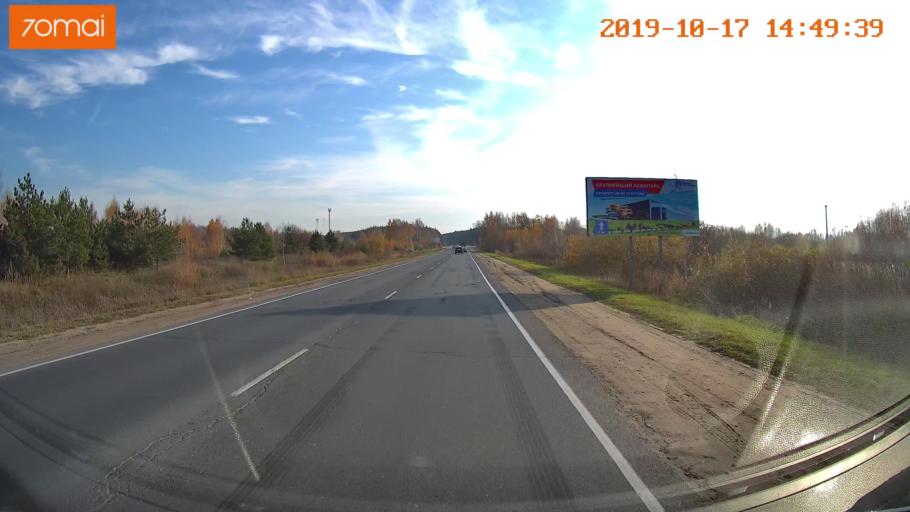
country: RU
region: Rjazan
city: Polyany
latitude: 54.7440
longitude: 39.8404
